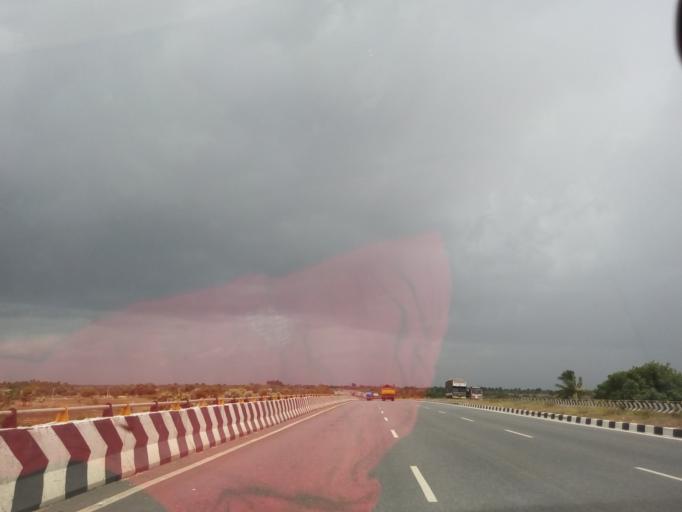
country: IN
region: Karnataka
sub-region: Chitradurga
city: Chitradurga
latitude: 14.1488
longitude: 76.4868
